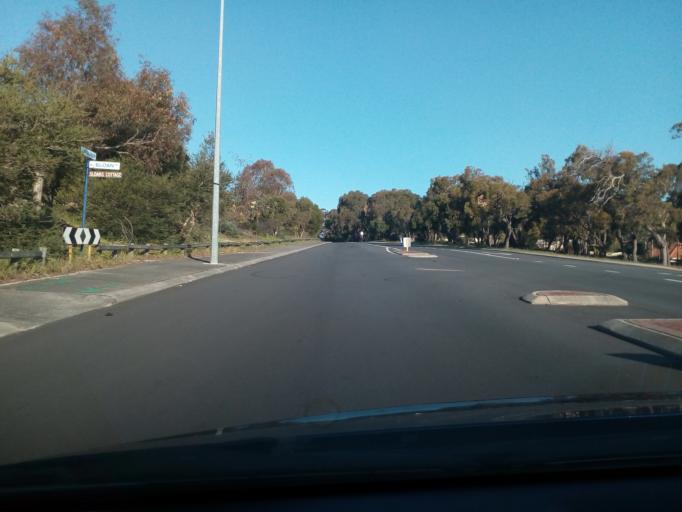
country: AU
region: Western Australia
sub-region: Kwinana
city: Parmelia
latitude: -32.2519
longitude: 115.8041
